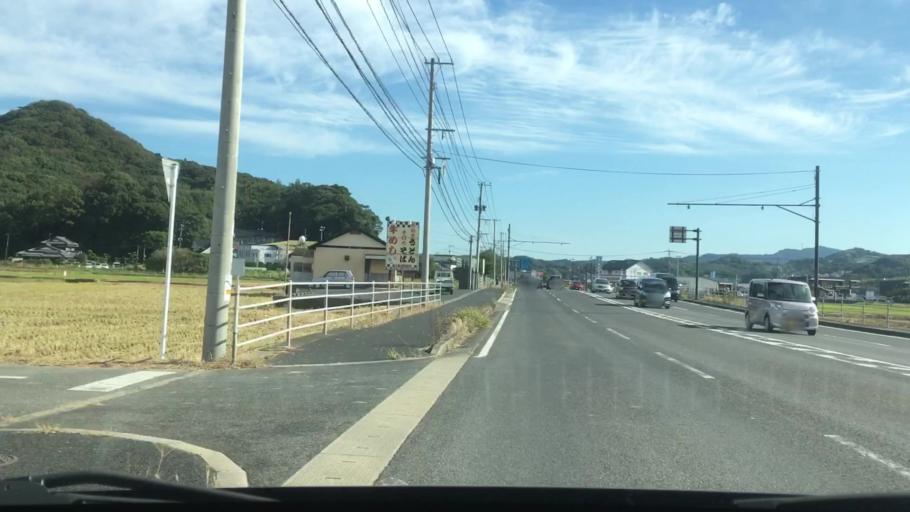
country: JP
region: Nagasaki
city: Sasebo
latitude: 33.1068
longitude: 129.7814
